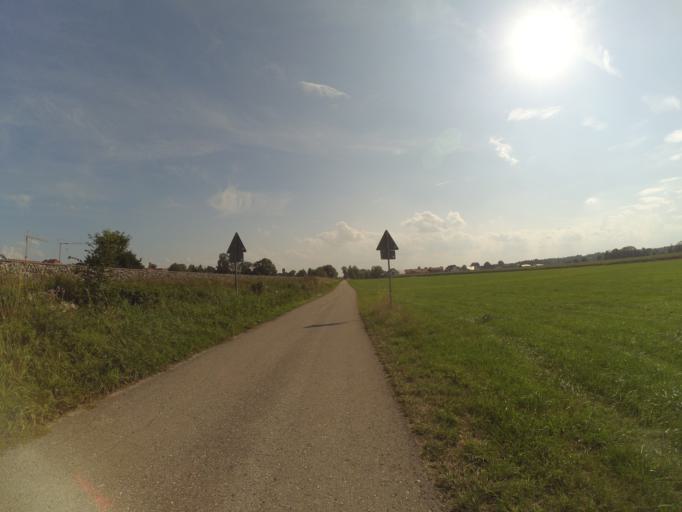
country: DE
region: Bavaria
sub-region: Swabia
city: Buchloe
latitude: 48.0650
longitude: 10.7281
